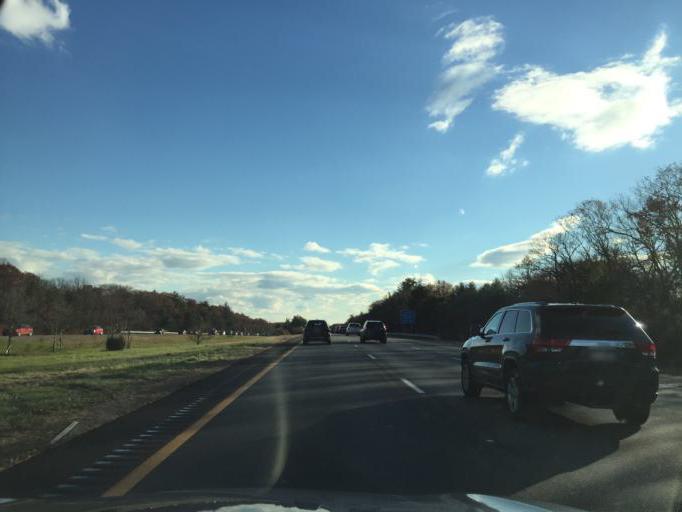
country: US
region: Massachusetts
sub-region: Norfolk County
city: Plainville
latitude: 41.9893
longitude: -71.2934
